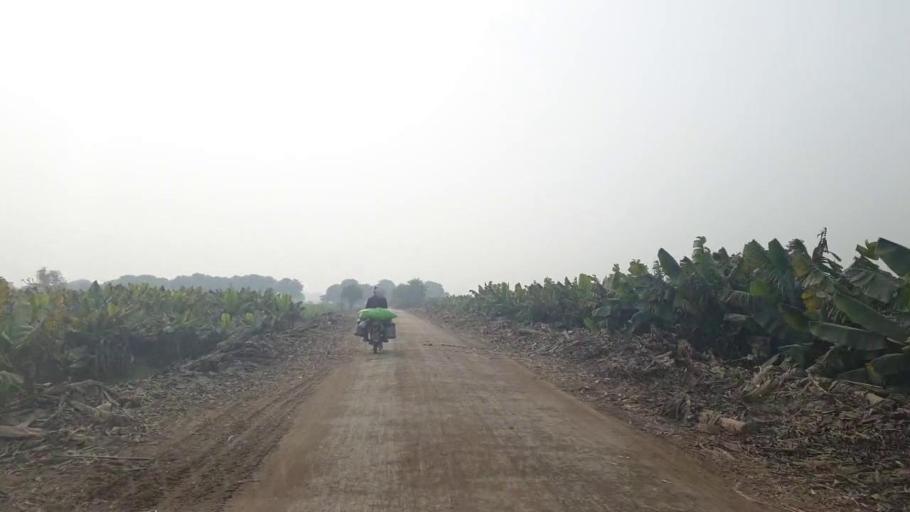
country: PK
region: Sindh
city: Tando Adam
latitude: 25.7140
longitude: 68.6263
